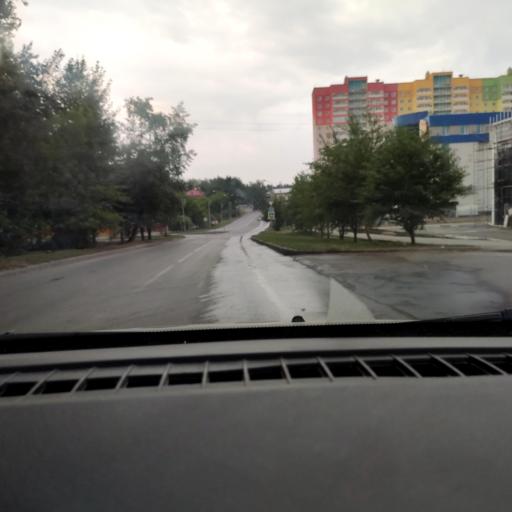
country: RU
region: Perm
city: Perm
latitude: 58.1103
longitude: 56.3041
